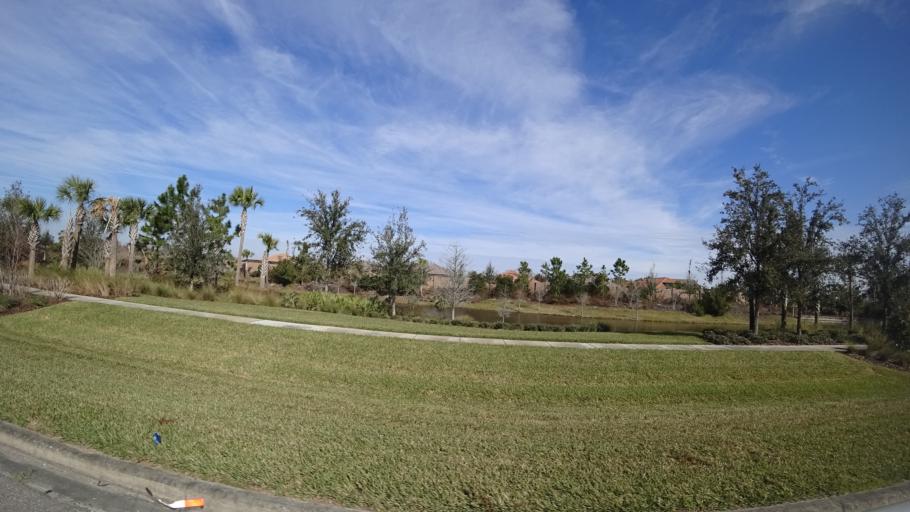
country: US
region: Florida
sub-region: Manatee County
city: Memphis
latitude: 27.6015
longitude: -82.5196
